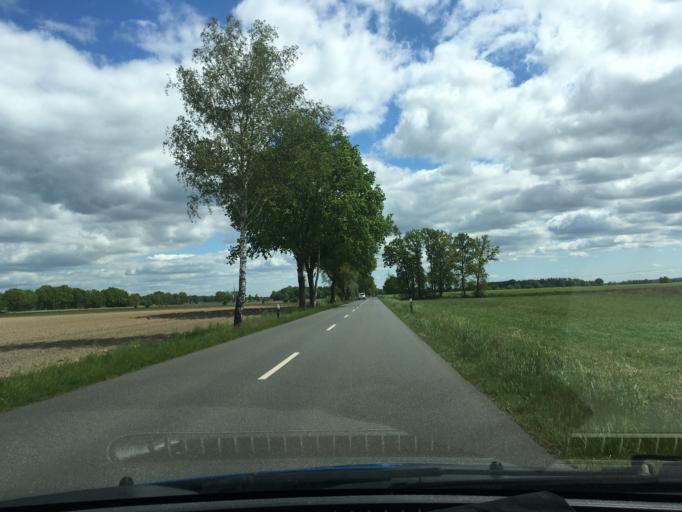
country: DE
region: Lower Saxony
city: Suderburg
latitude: 52.9297
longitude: 10.4560
